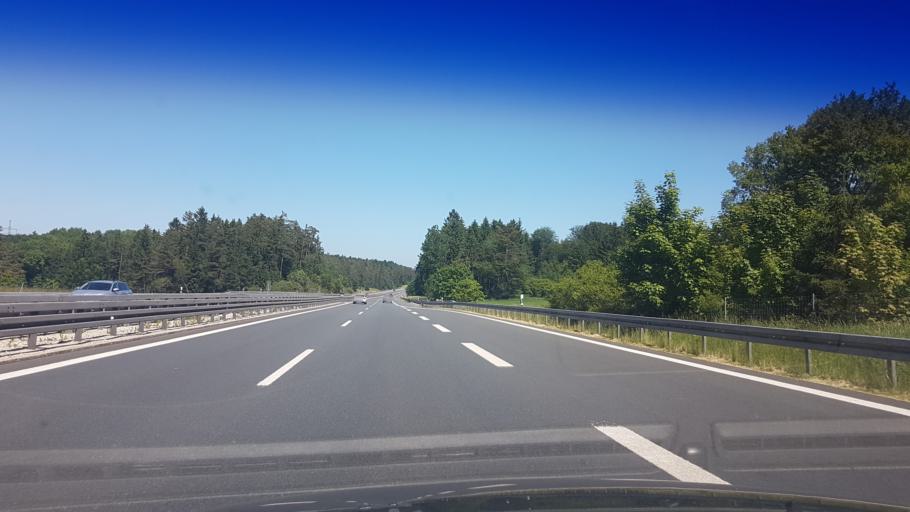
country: DE
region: Bavaria
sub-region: Upper Franconia
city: Stadelhofen
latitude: 49.9949
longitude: 11.1717
